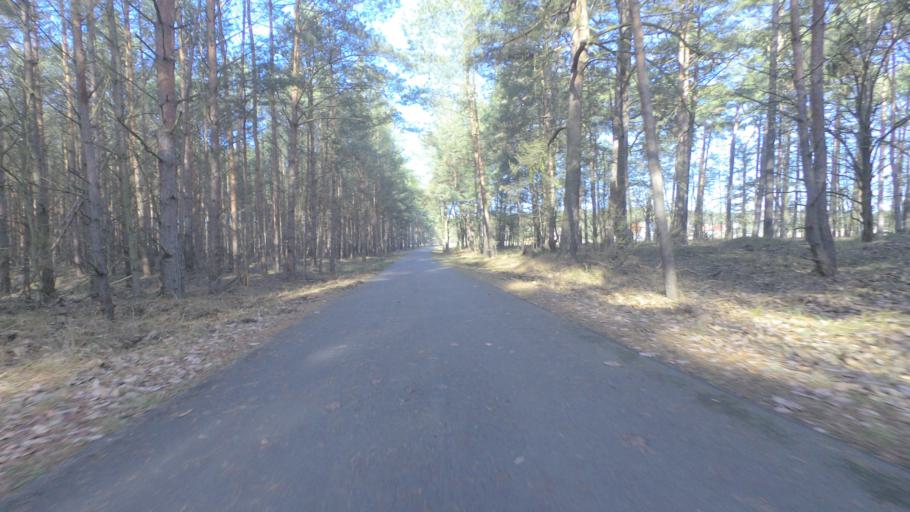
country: DE
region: Brandenburg
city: Luckenwalde
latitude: 52.0536
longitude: 13.1543
